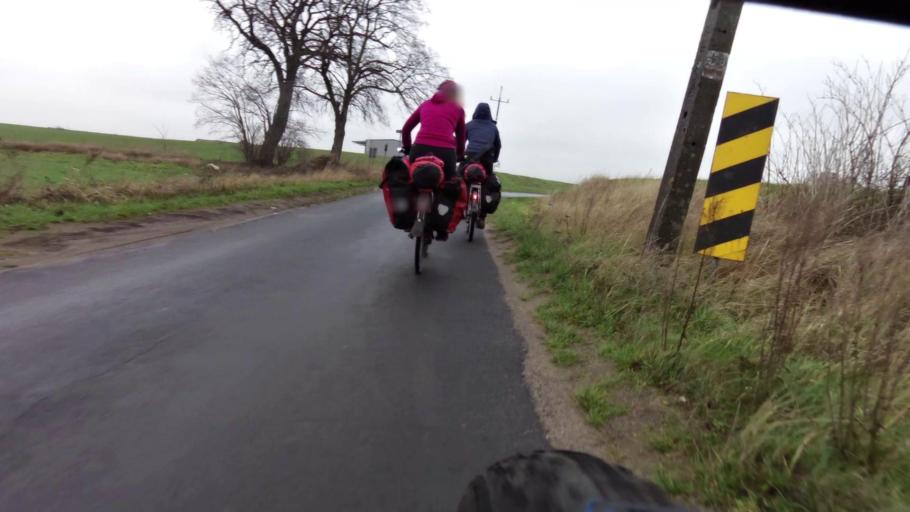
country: PL
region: Lubusz
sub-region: Powiat gorzowski
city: Kostrzyn nad Odra
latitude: 52.6479
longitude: 14.7150
